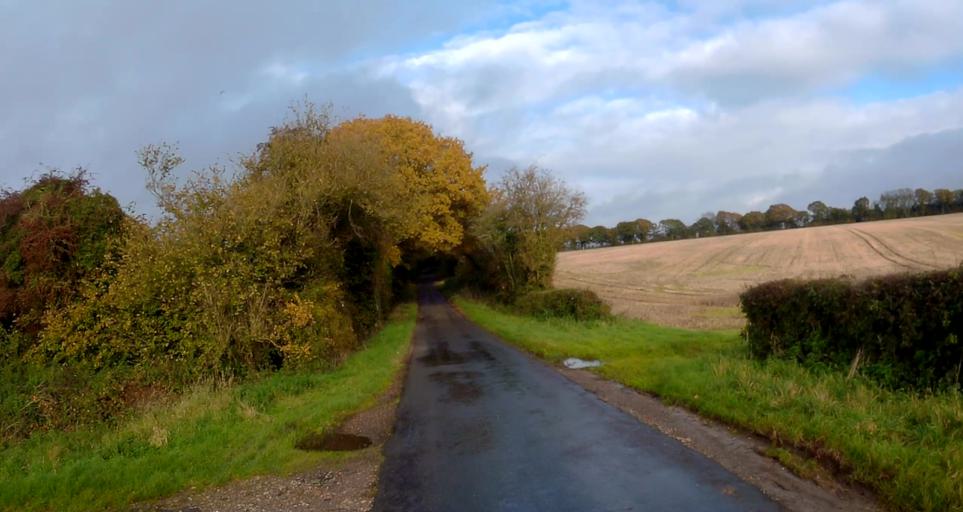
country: GB
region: England
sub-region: Hampshire
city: Four Marks
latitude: 51.1466
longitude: -1.0932
